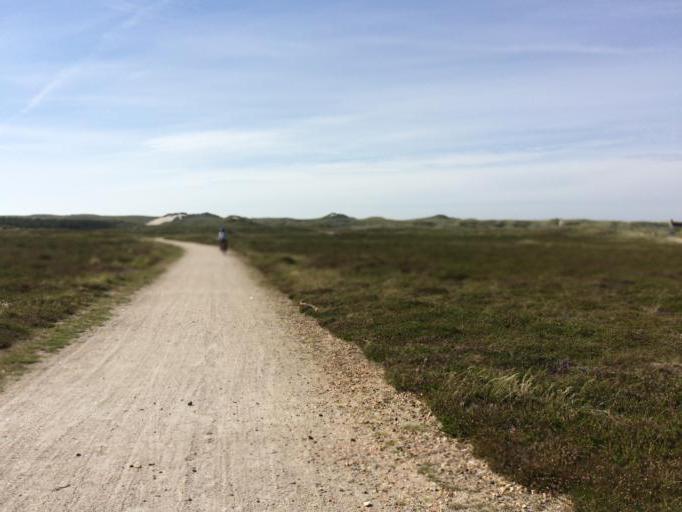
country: DK
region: Central Jutland
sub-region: Ringkobing-Skjern Kommune
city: Hvide Sande
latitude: 55.8595
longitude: 8.1695
